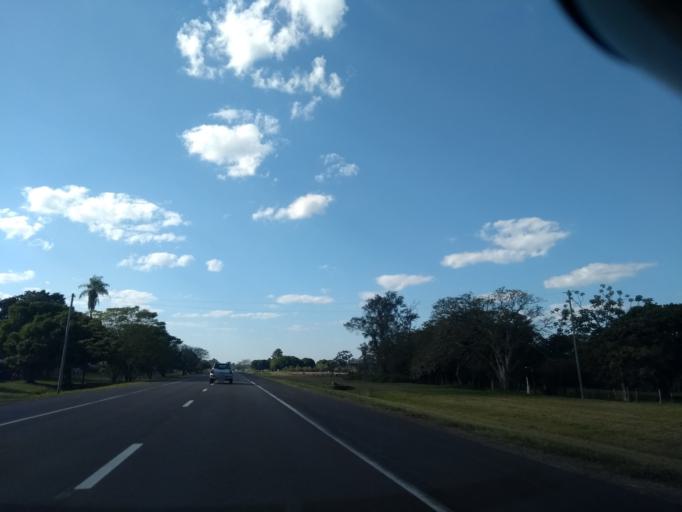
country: AR
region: Corrientes
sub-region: Departamento de San Cosme
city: San Cosme
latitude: -27.3660
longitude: -58.4332
